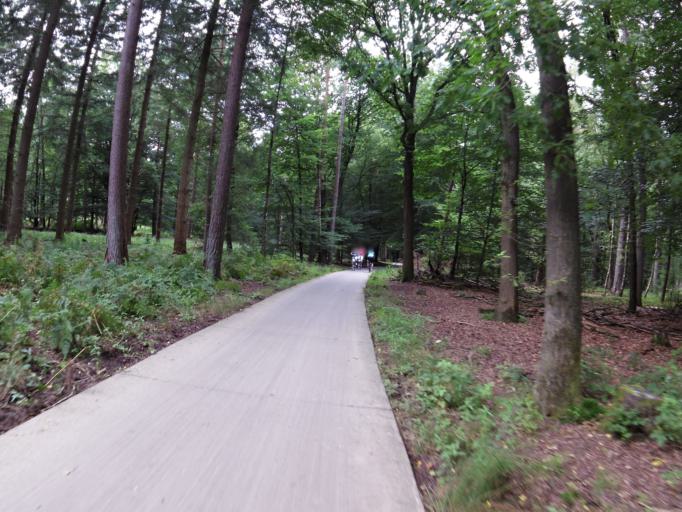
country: NL
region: Gelderland
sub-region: Gemeente Rheden
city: De Steeg
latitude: 52.0309
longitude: 6.0454
